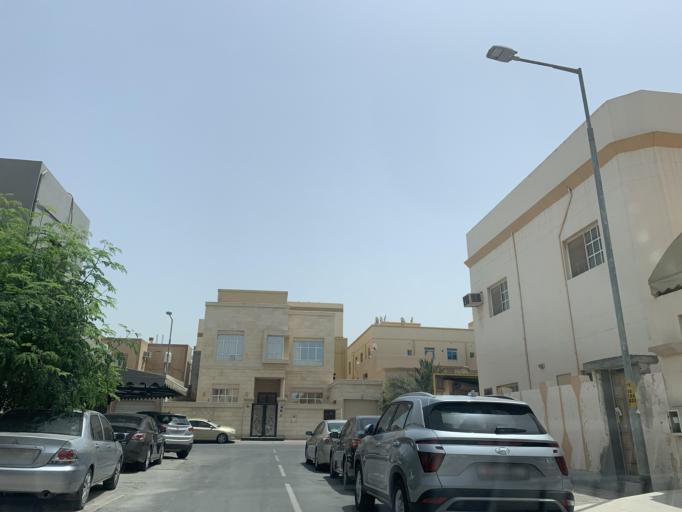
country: BH
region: Northern
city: Ar Rifa'
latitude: 26.1487
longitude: 50.5848
